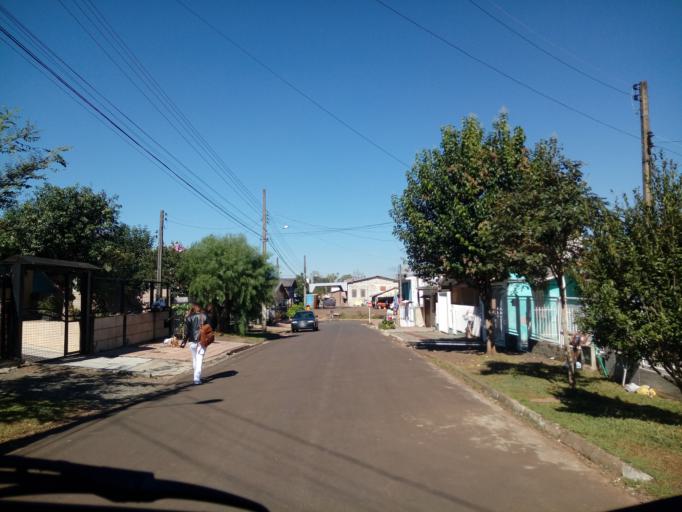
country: BR
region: Santa Catarina
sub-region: Chapeco
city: Chapeco
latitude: -27.0932
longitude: -52.6821
